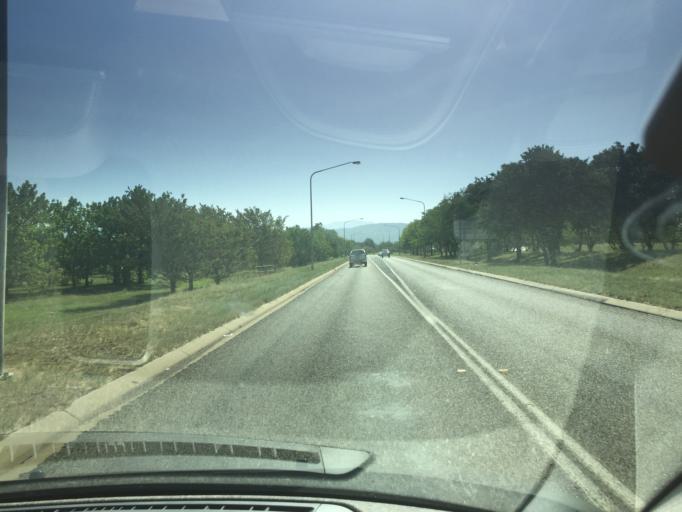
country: AU
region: Australian Capital Territory
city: Macarthur
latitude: -35.4212
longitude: 149.1007
